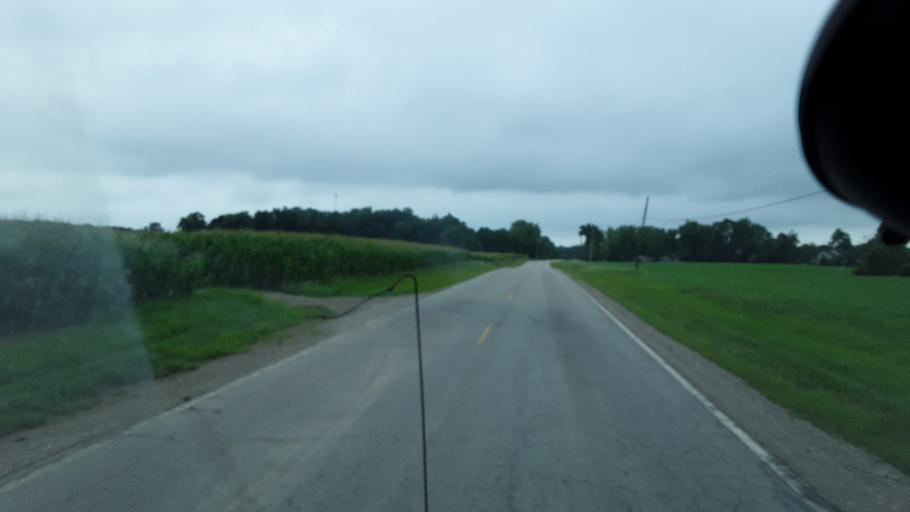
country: US
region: Indiana
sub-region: Wells County
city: Bluffton
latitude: 40.7167
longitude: -85.0891
